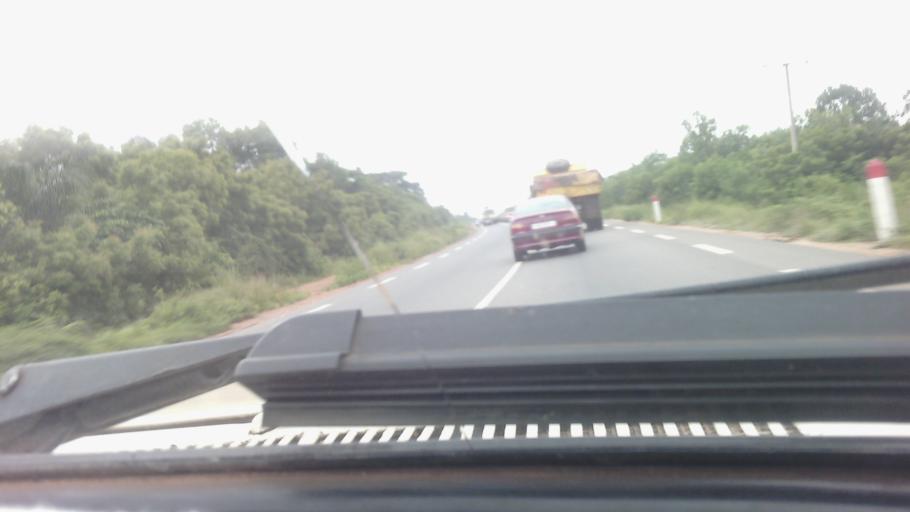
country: BJ
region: Atlantique
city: Ouidah
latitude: 6.3691
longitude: 2.0376
